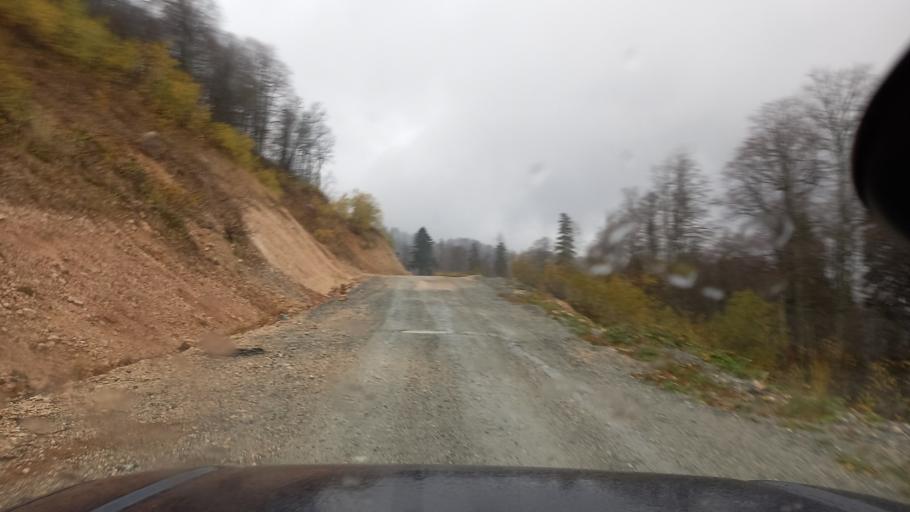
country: RU
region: Krasnodarskiy
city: Dagomys
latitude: 43.9829
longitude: 39.8504
